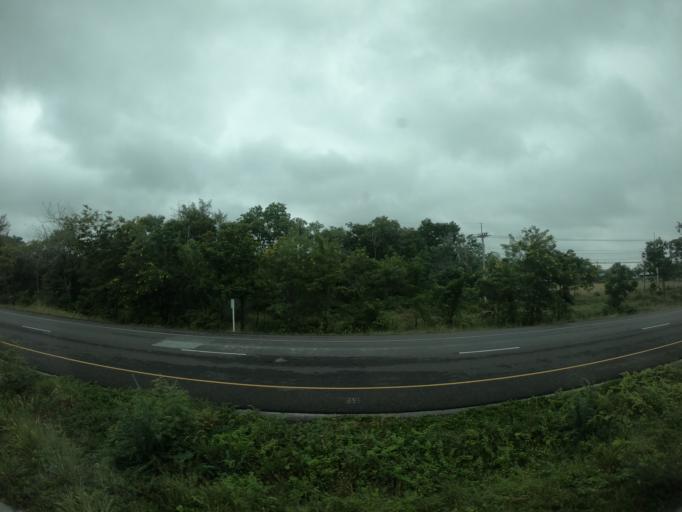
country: TH
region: Nakhon Ratchasima
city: Non Daeng
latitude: 15.4549
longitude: 102.5011
